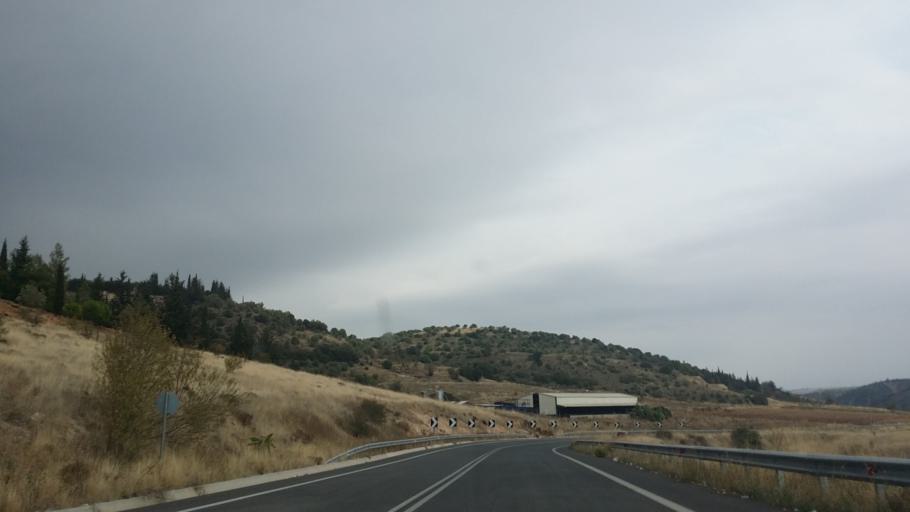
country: GR
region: Central Greece
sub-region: Nomos Voiotias
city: Vagia
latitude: 38.2989
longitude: 23.1908
